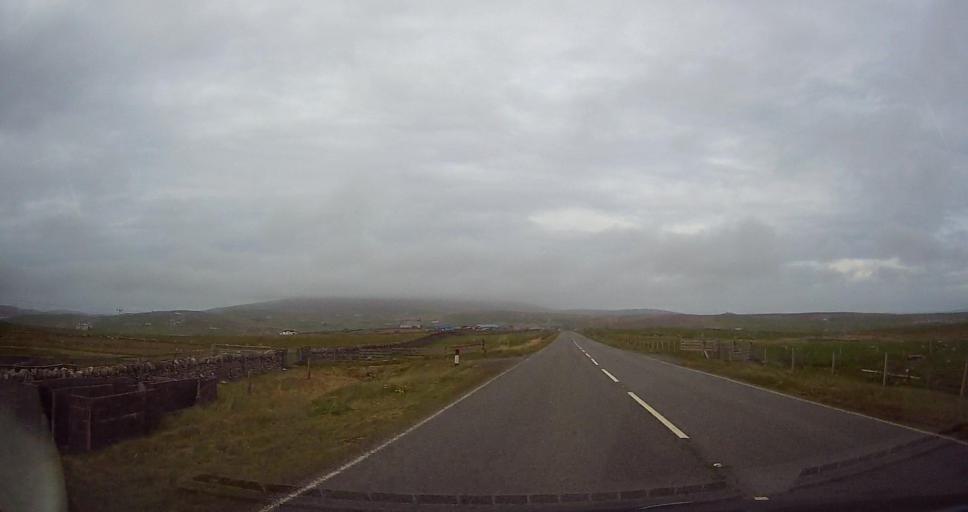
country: GB
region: Scotland
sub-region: Shetland Islands
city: Sandwick
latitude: 59.9138
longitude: -1.3016
